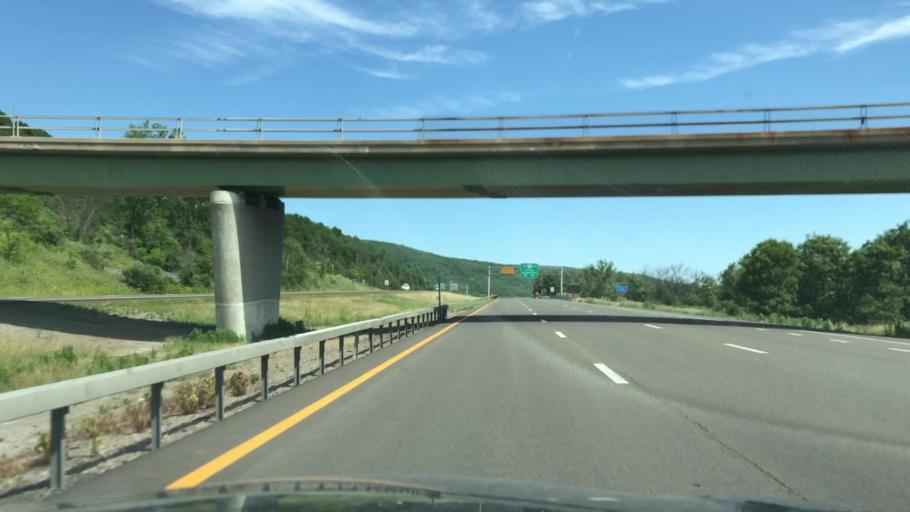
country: US
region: New York
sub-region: Steuben County
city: Bath
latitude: 42.3872
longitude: -77.3807
